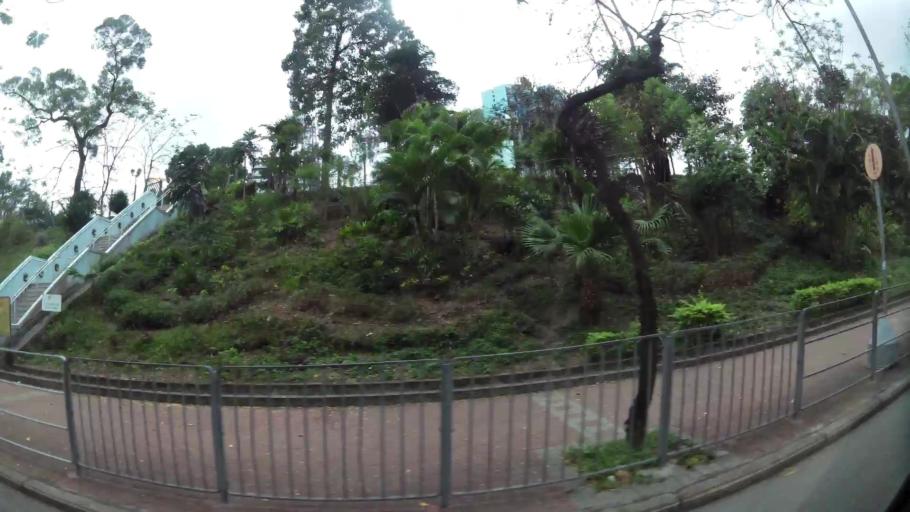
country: HK
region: Wong Tai Sin
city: Wong Tai Sin
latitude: 22.3360
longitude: 114.1914
